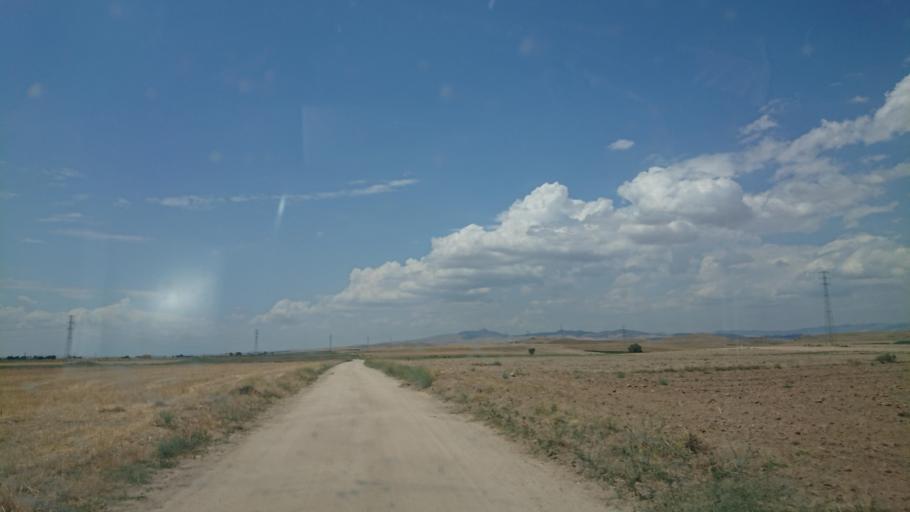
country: TR
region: Aksaray
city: Sariyahsi
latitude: 39.0050
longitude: 33.8854
